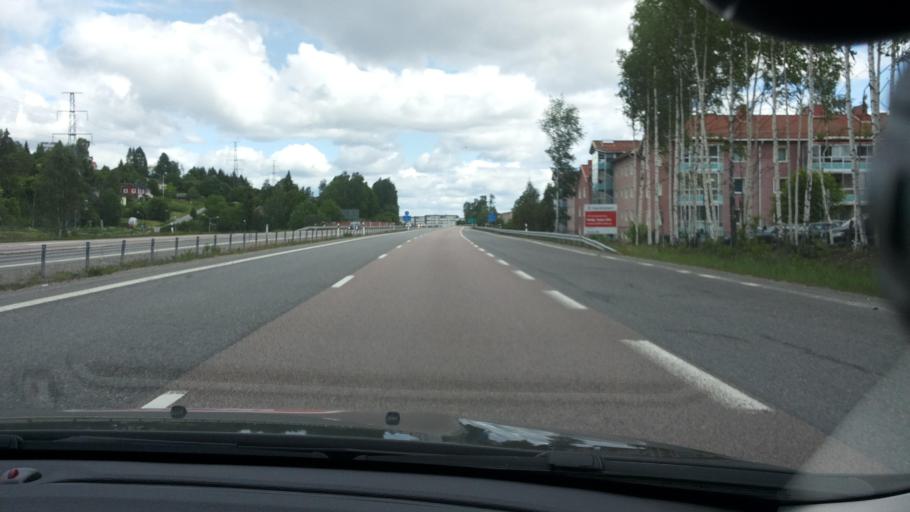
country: SE
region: Vaesternorrland
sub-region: Timra Kommun
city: Timra
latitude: 62.4808
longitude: 17.3155
